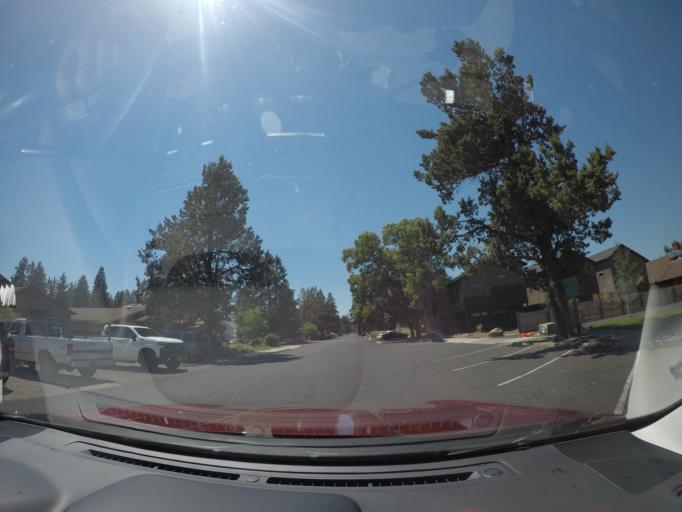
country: US
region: Oregon
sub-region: Deschutes County
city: Sisters
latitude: 44.2897
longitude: -121.5442
